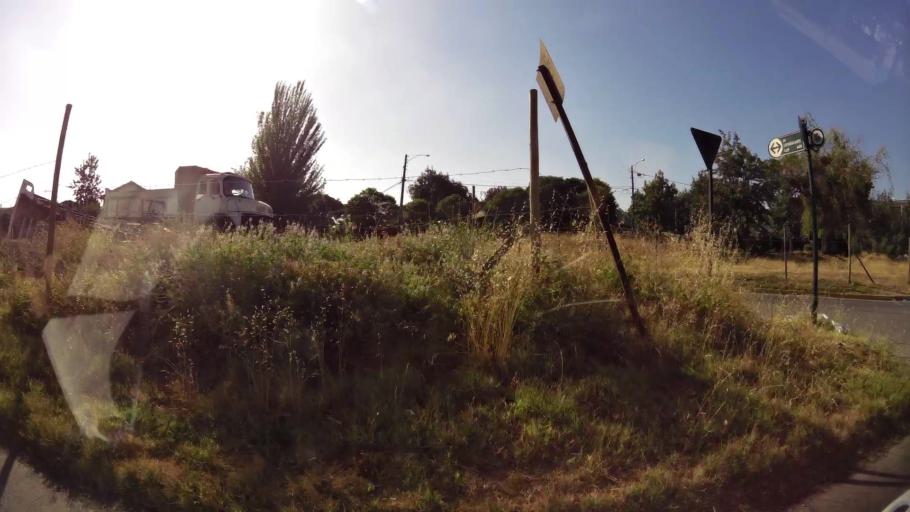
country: CL
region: Maule
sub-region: Provincia de Talca
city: Talca
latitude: -35.4187
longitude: -71.6694
